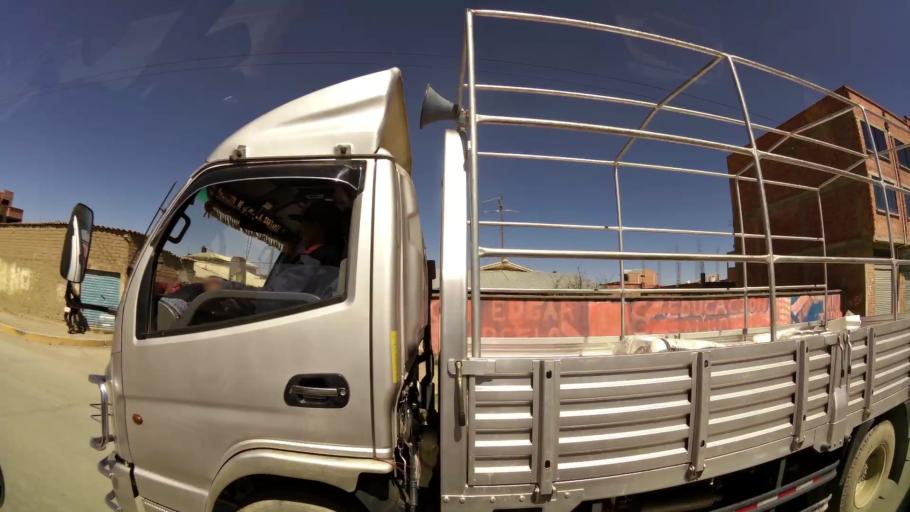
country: BO
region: La Paz
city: La Paz
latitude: -16.5029
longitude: -68.2232
